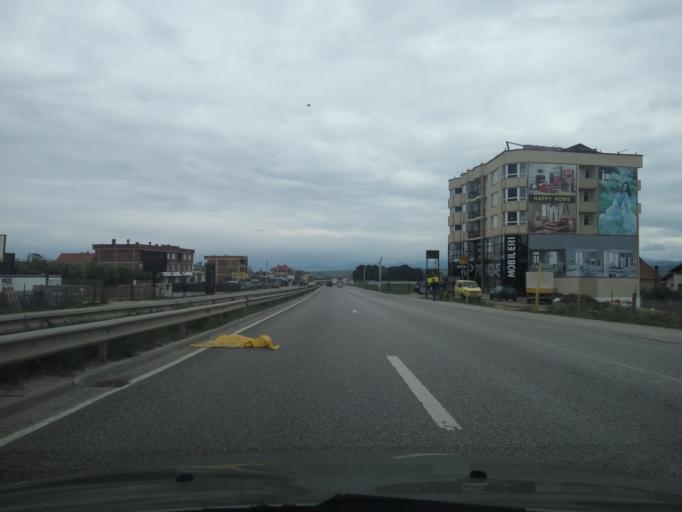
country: XK
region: Pristina
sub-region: Kosovo Polje
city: Kosovo Polje
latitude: 42.6962
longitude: 21.1150
